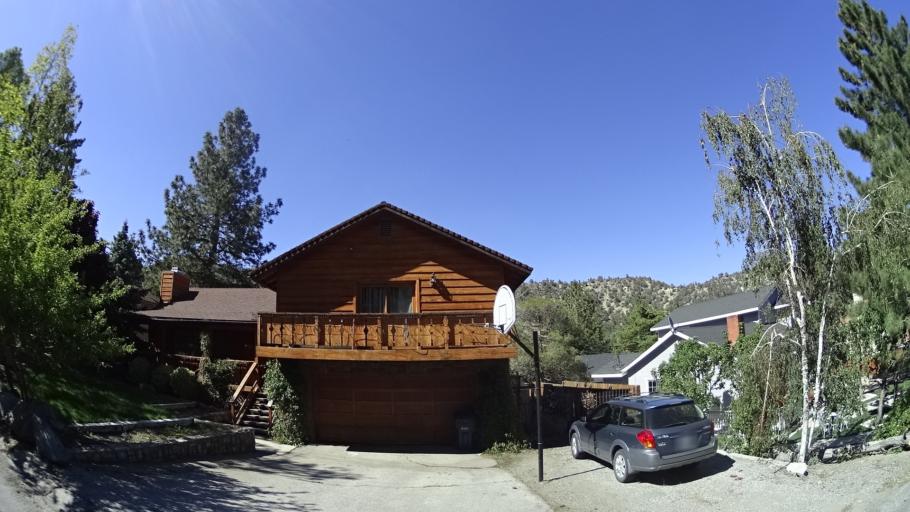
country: US
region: California
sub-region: San Bernardino County
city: Wrightwood
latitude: 34.3632
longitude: -117.6454
